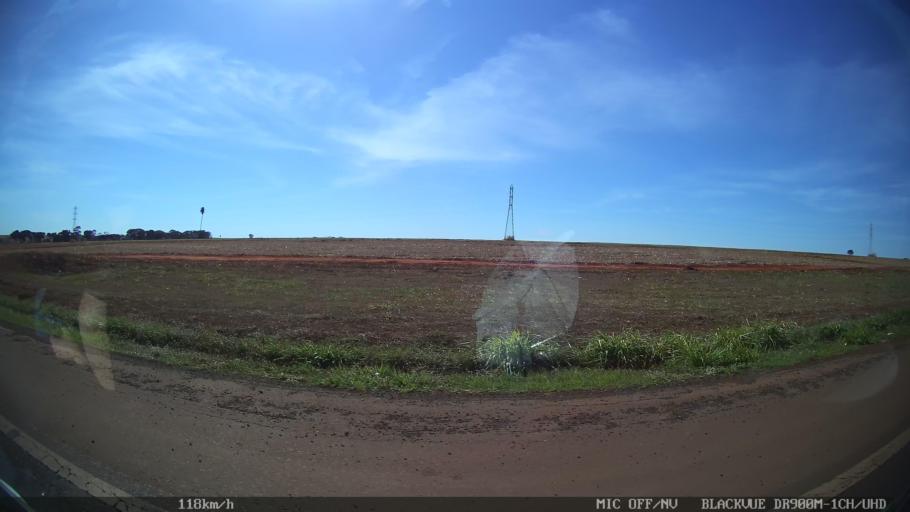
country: BR
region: Sao Paulo
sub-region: Ipua
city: Ipua
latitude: -20.4620
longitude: -48.1385
